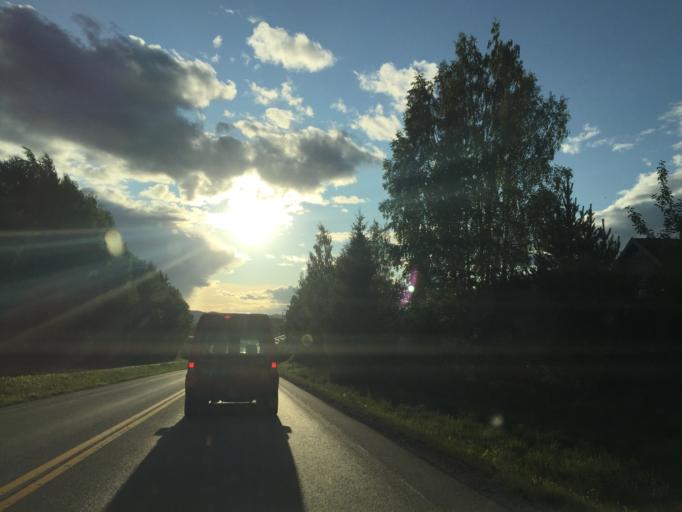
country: NO
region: Akershus
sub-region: Fet
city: Fetsund
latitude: 59.9227
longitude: 11.1746
